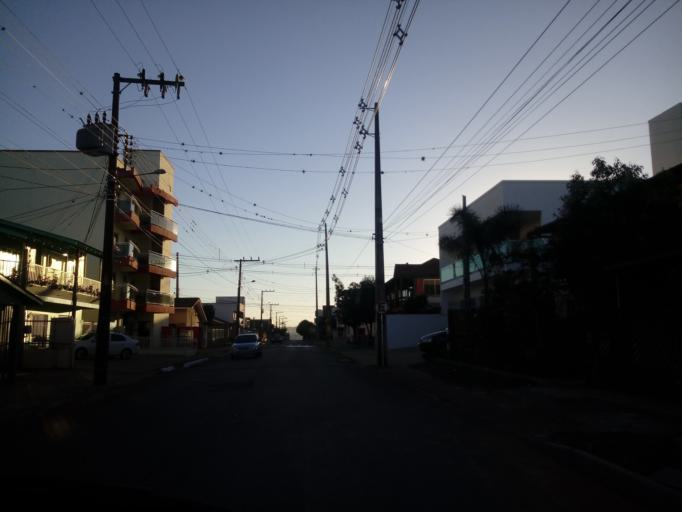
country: BR
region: Santa Catarina
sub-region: Chapeco
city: Chapeco
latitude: -27.0871
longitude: -52.6301
